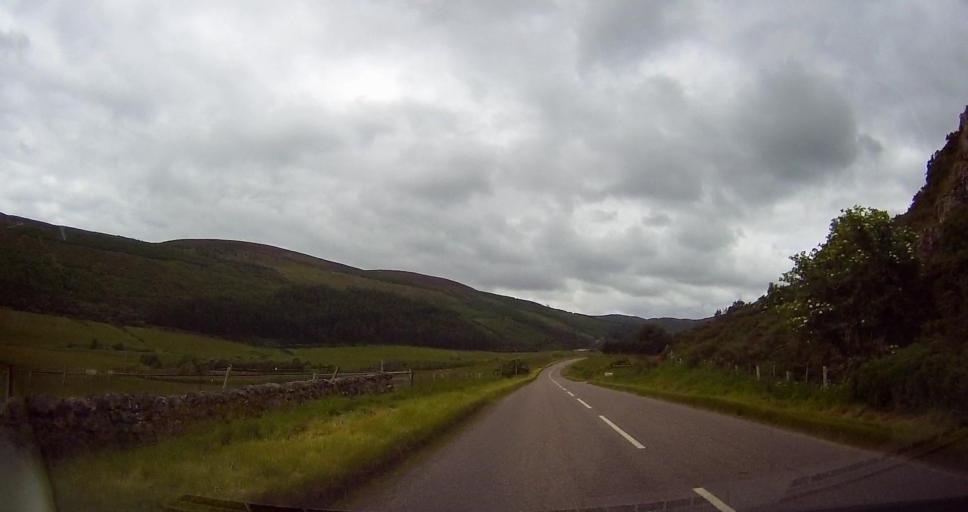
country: GB
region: Scotland
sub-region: Highland
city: Dornoch
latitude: 57.9836
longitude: -4.1395
